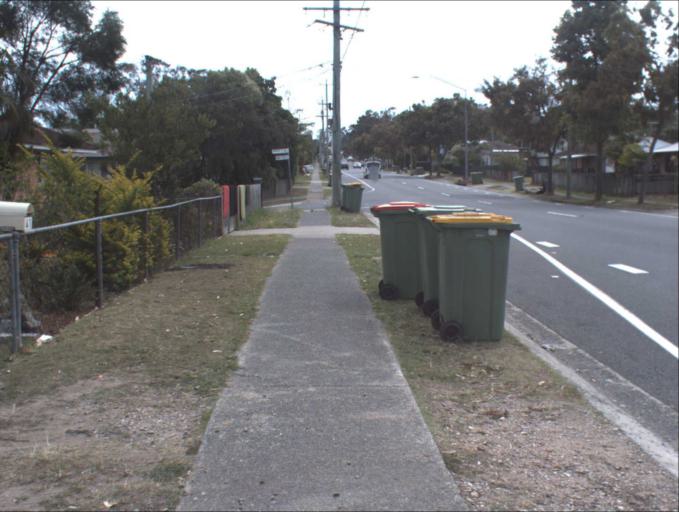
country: AU
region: Queensland
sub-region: Logan
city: Springwood
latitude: -27.6272
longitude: 153.1233
